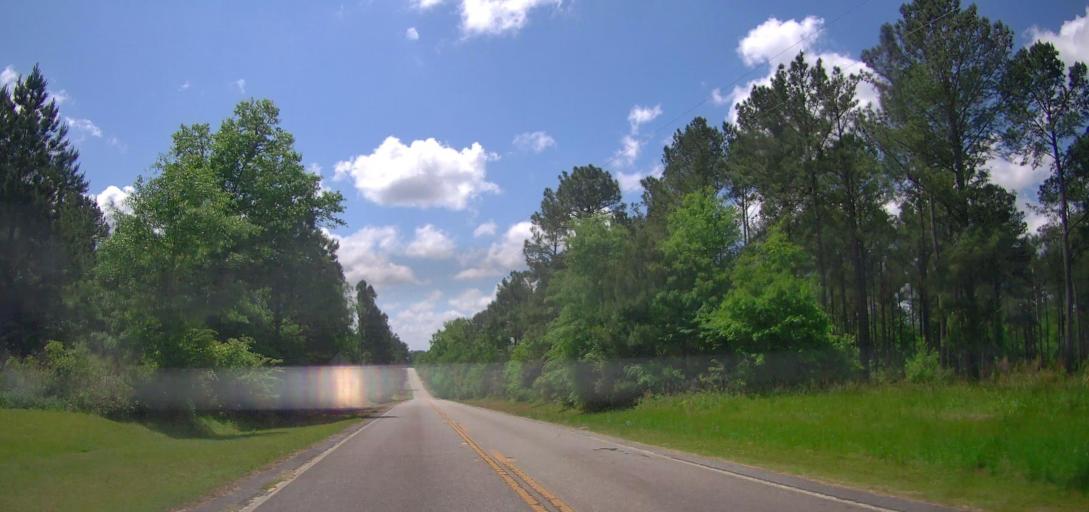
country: US
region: Georgia
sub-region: Bleckley County
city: Cochran
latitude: 32.4576
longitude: -83.2863
